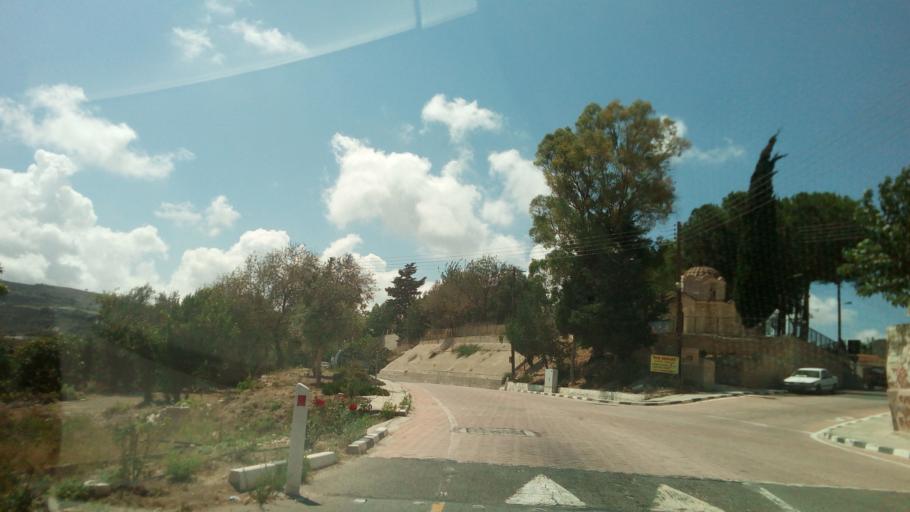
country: CY
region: Pafos
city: Tala
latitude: 34.8894
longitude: 32.4801
